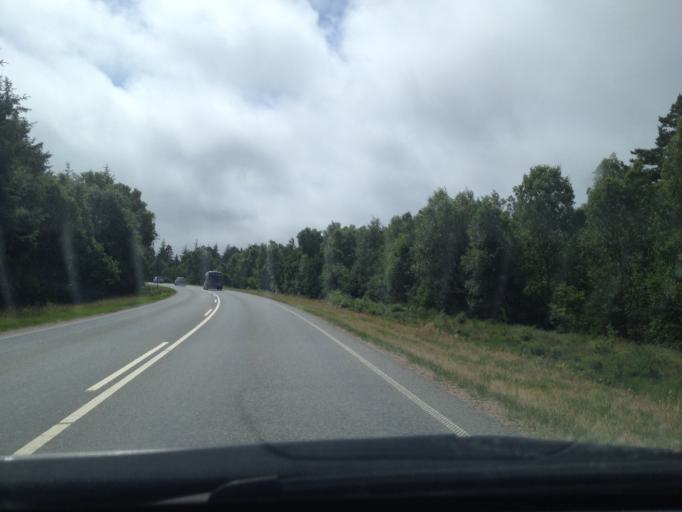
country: DK
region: South Denmark
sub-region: Varde Kommune
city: Oksbol
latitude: 55.6019
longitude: 8.2246
